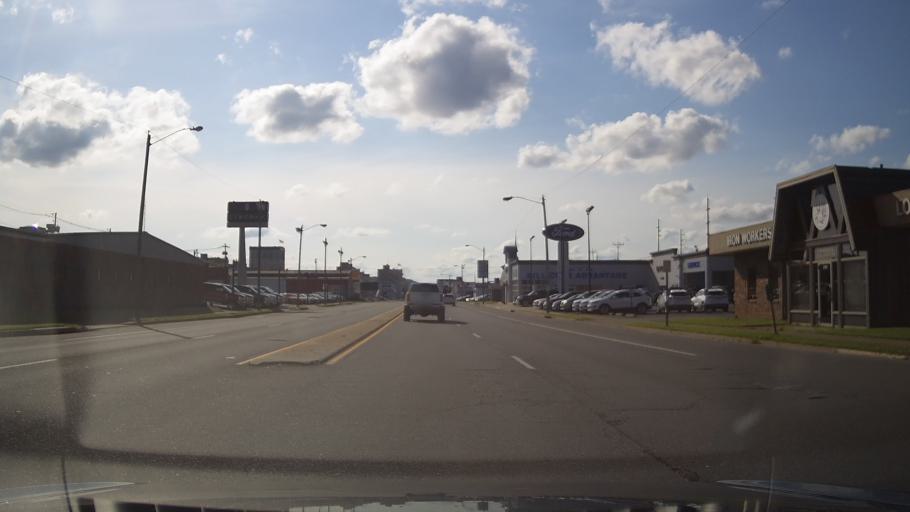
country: US
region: Kentucky
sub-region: Boyd County
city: Ashland
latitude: 38.4759
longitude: -82.6315
